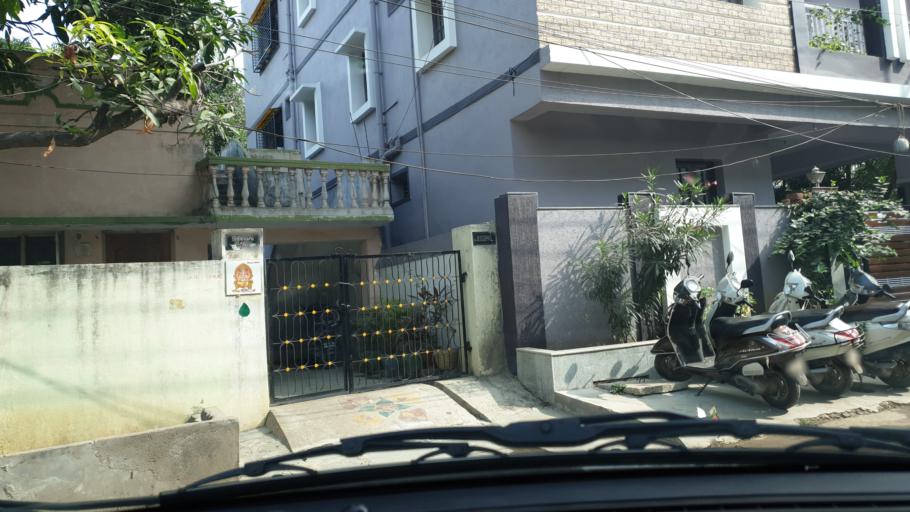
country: IN
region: Telangana
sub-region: Rangareddi
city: Kukatpalli
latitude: 17.4859
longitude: 78.4055
